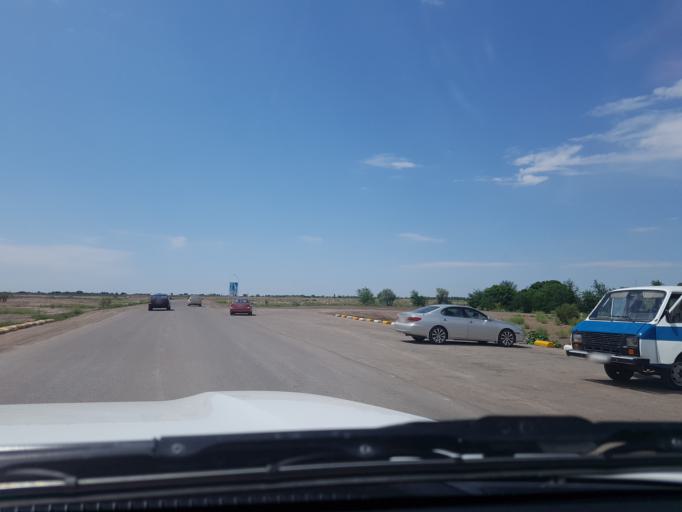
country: TM
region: Dasoguz
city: Koeneuergench
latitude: 42.3105
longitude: 59.1377
